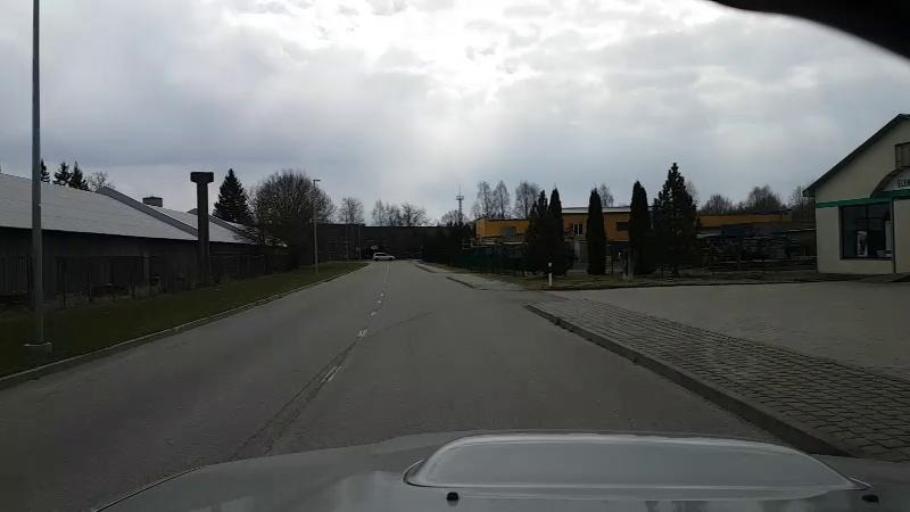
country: EE
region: Jaervamaa
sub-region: Paide linn
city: Paide
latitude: 58.8823
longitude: 25.5573
